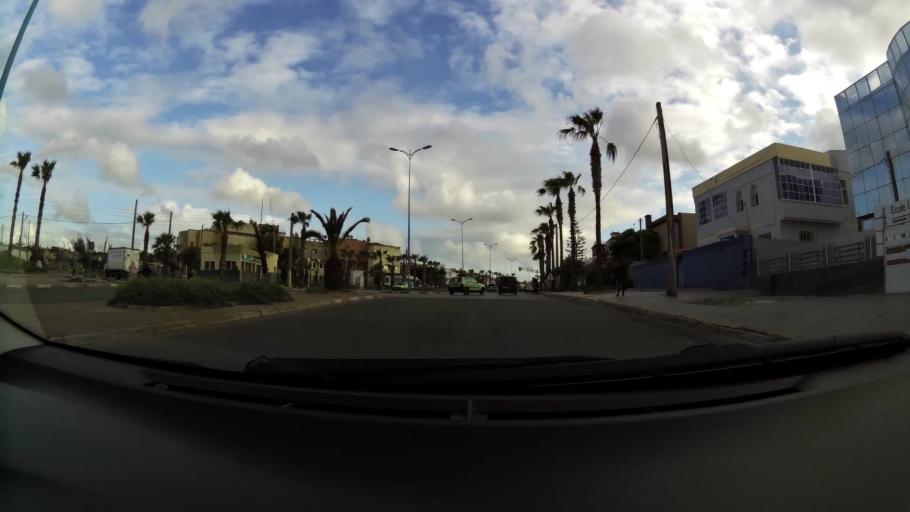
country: MA
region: Grand Casablanca
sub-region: Mohammedia
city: Mohammedia
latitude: 33.7003
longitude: -7.3707
